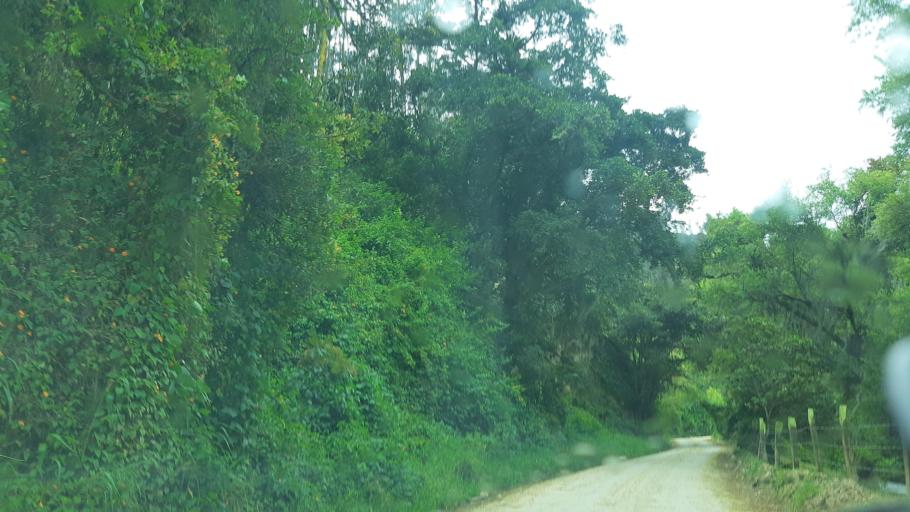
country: CO
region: Boyaca
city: Turmeque
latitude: 5.3269
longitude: -73.4478
